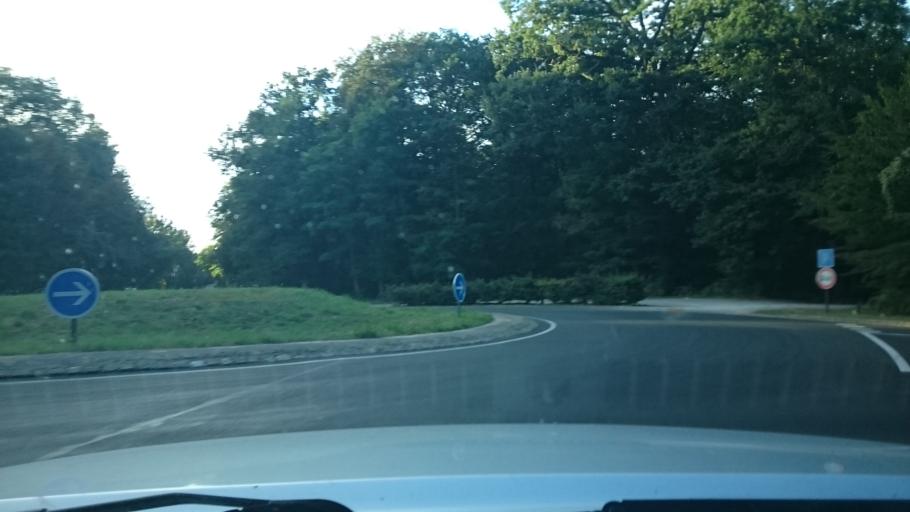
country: FR
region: Ile-de-France
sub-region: Departement de Seine-et-Marne
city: Samoreau
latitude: 48.4049
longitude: 2.7528
